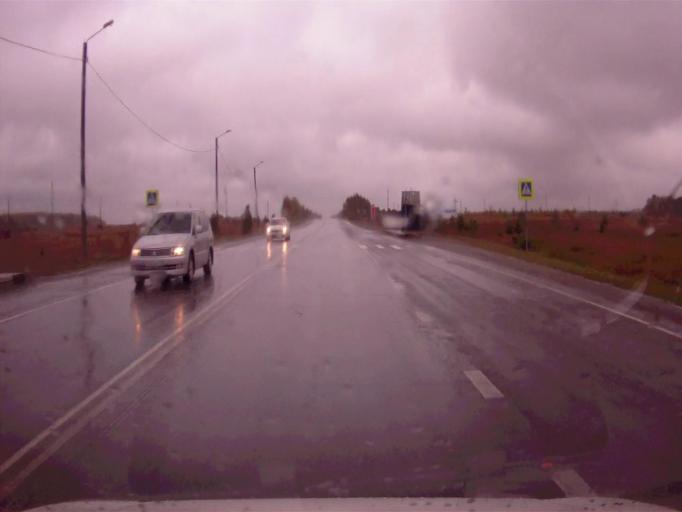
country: RU
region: Chelyabinsk
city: Argayash
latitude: 55.4776
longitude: 60.8563
